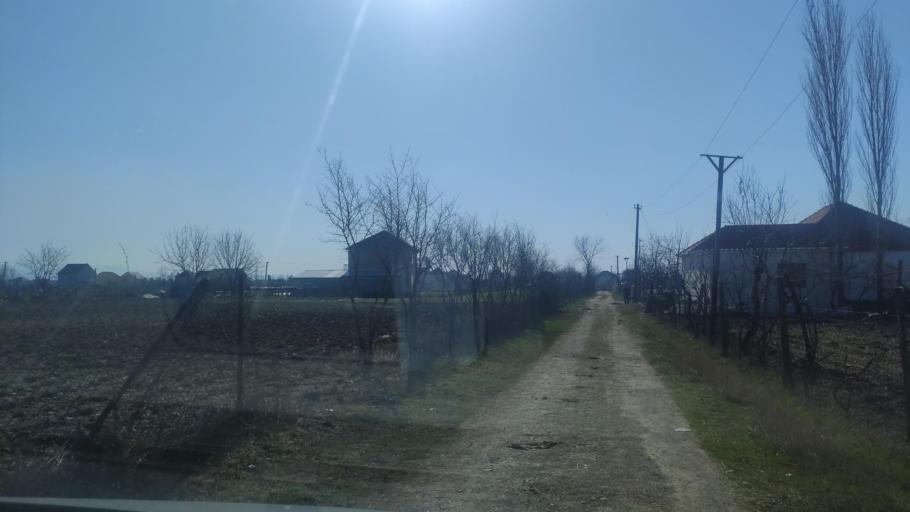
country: AL
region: Shkoder
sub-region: Rrethi i Malesia e Madhe
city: Grude-Fushe
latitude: 42.1660
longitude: 19.4577
